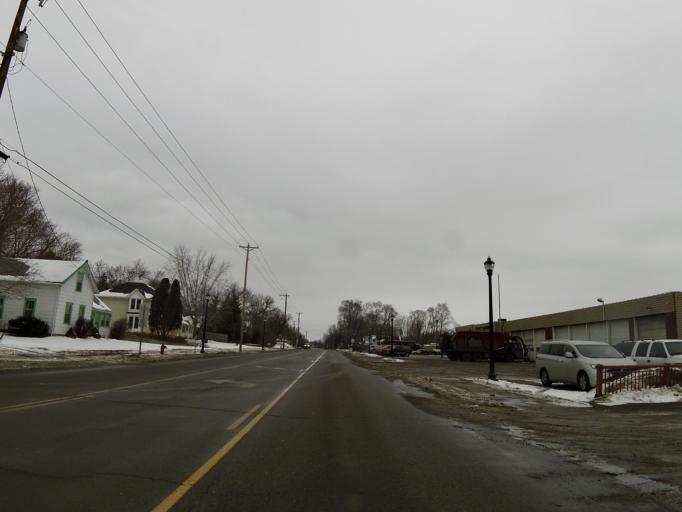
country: US
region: Minnesota
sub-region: Washington County
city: Newport
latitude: 44.8607
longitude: -93.0217
